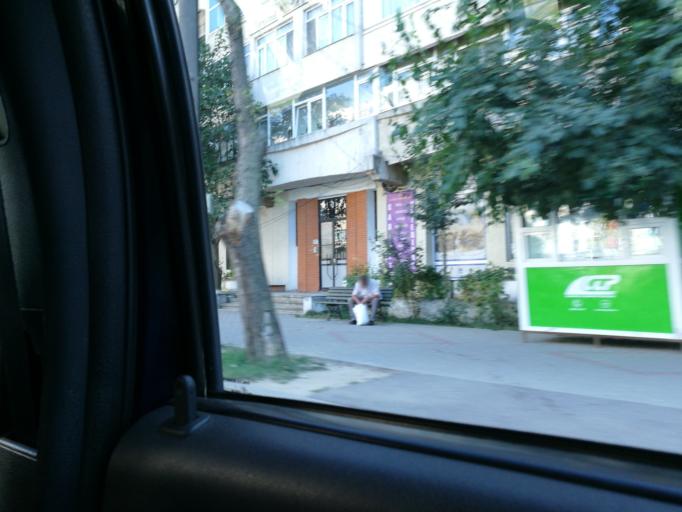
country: RO
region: Iasi
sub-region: Municipiul Iasi
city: Iasi
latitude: 47.1709
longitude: 27.5613
